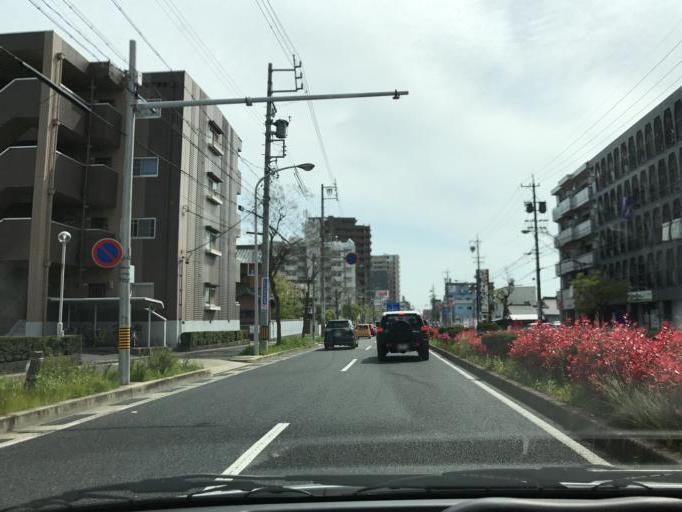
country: JP
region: Aichi
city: Nagoya-shi
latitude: 35.1043
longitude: 136.9572
